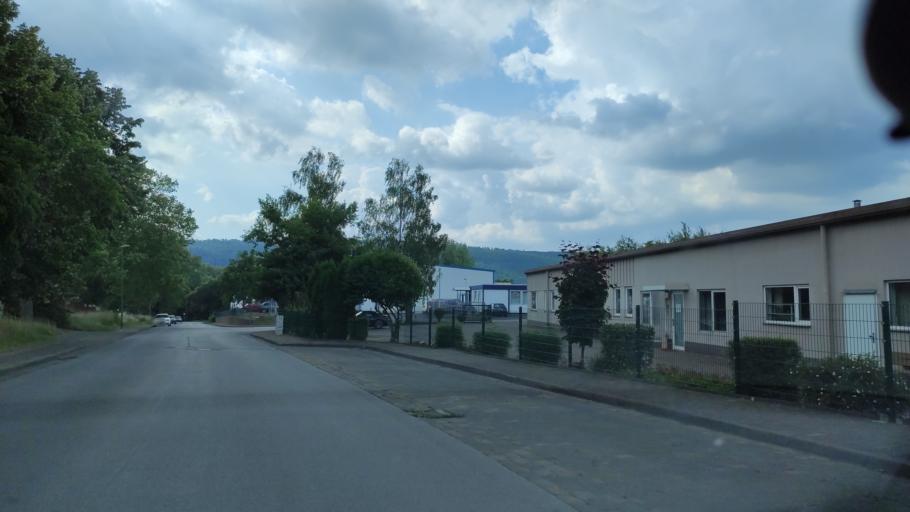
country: DE
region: Lower Saxony
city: Holzminden
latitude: 51.8390
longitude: 9.4636
